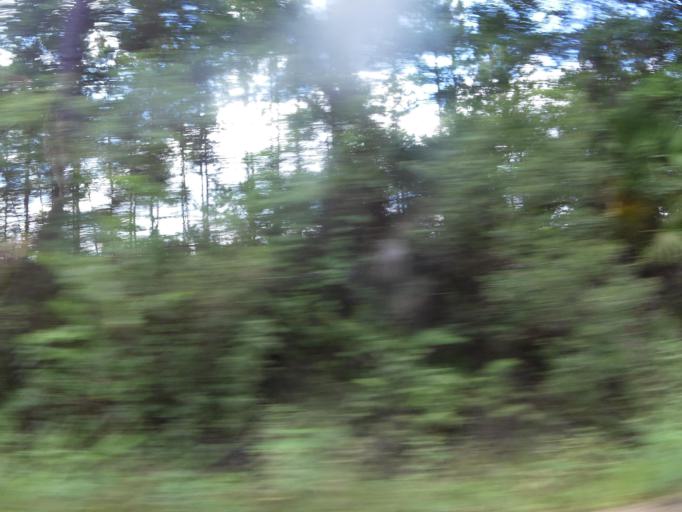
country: US
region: Florida
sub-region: Clay County
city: Asbury Lake
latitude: 29.8961
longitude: -81.8589
